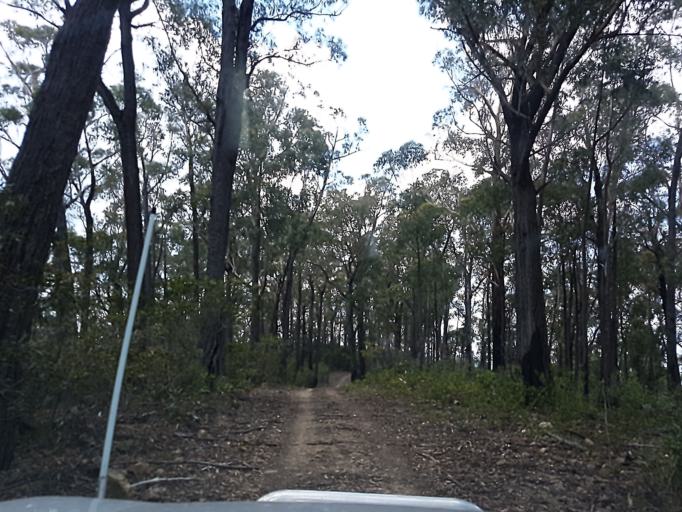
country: AU
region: Victoria
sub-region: East Gippsland
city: Lakes Entrance
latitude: -37.3458
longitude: 148.3390
